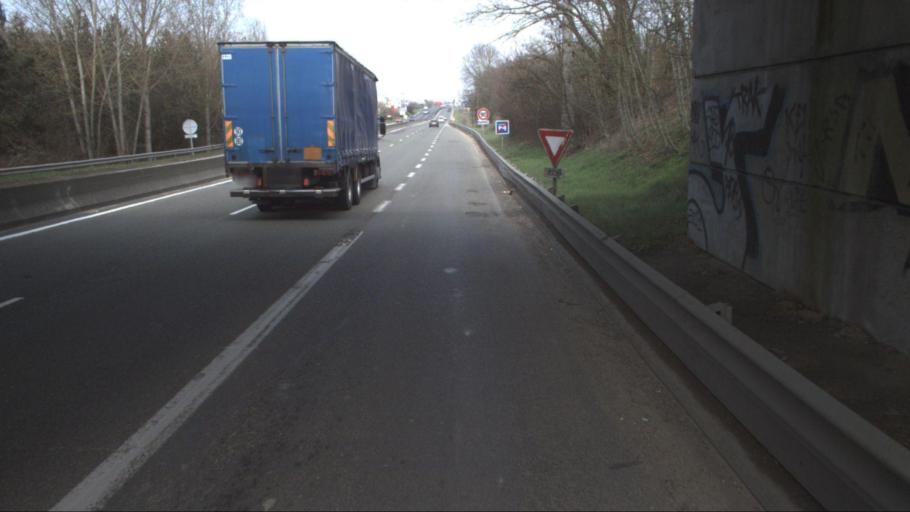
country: FR
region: Ile-de-France
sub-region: Departement des Yvelines
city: Rambouillet
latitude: 48.6203
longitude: 1.8312
